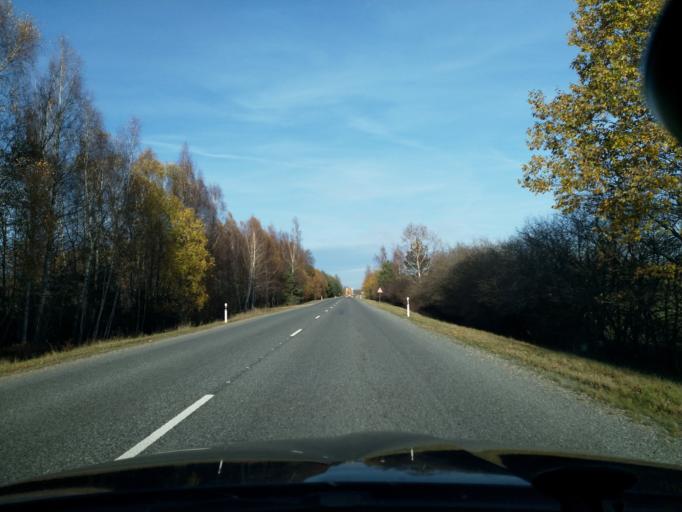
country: LV
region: Kuldigas Rajons
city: Kuldiga
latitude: 56.9511
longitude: 21.9389
